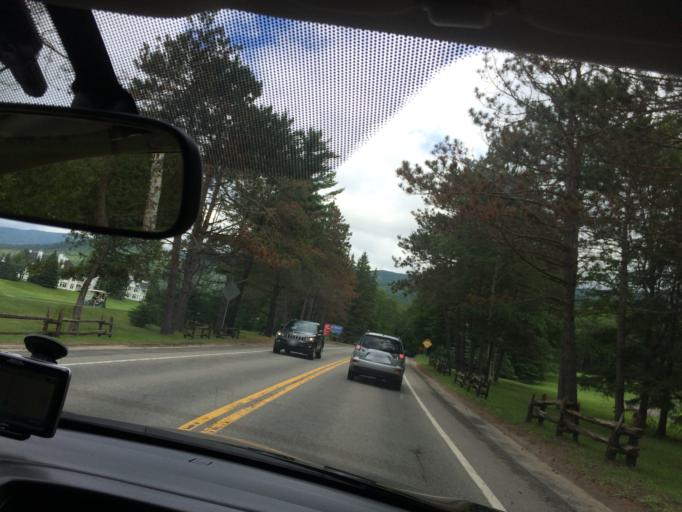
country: CA
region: Quebec
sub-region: Laurentides
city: Mont-Tremblant
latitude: 46.2025
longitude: -74.5953
